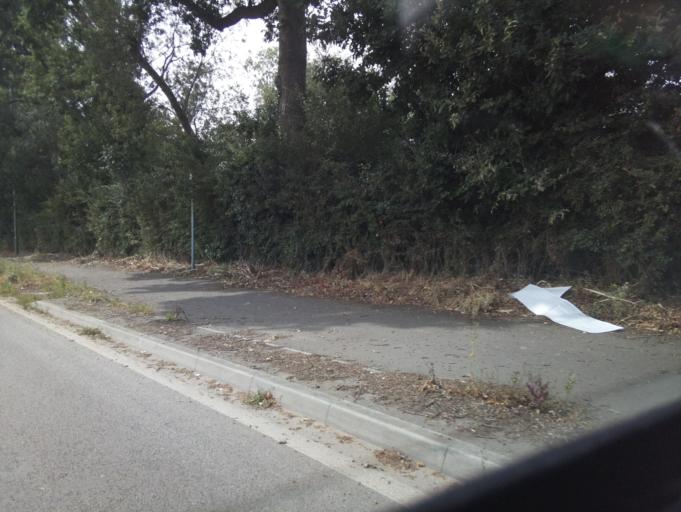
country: GB
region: England
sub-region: Surrey
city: Salfords
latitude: 51.1896
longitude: -0.1964
